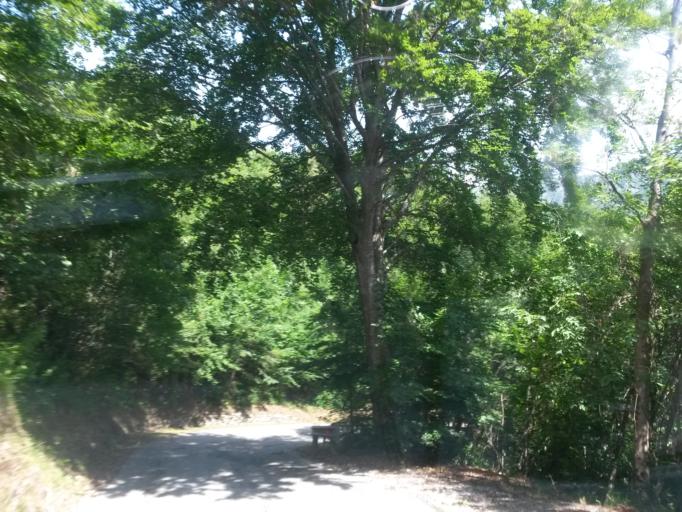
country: IT
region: Lombardy
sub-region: Provincia di Brescia
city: Gardola
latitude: 45.7770
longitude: 10.7148
